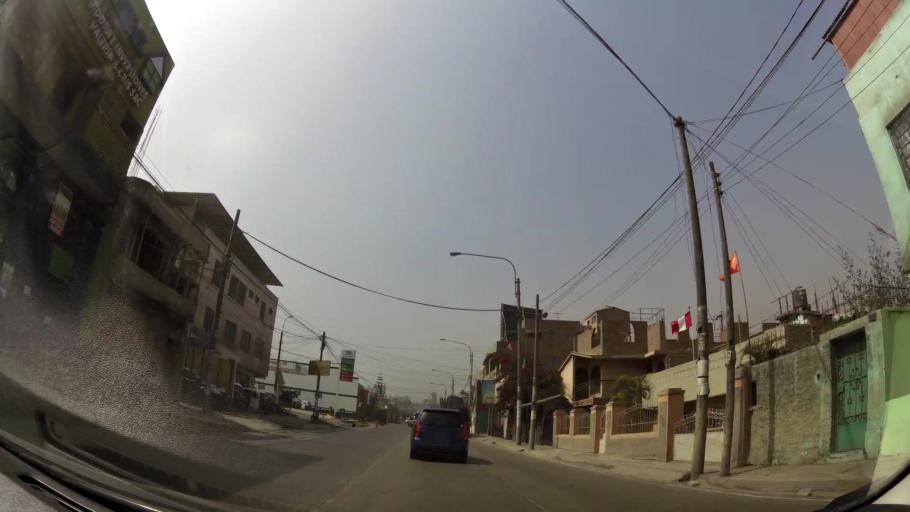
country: PE
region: Lima
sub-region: Lima
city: Chosica
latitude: -11.9435
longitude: -76.7076
